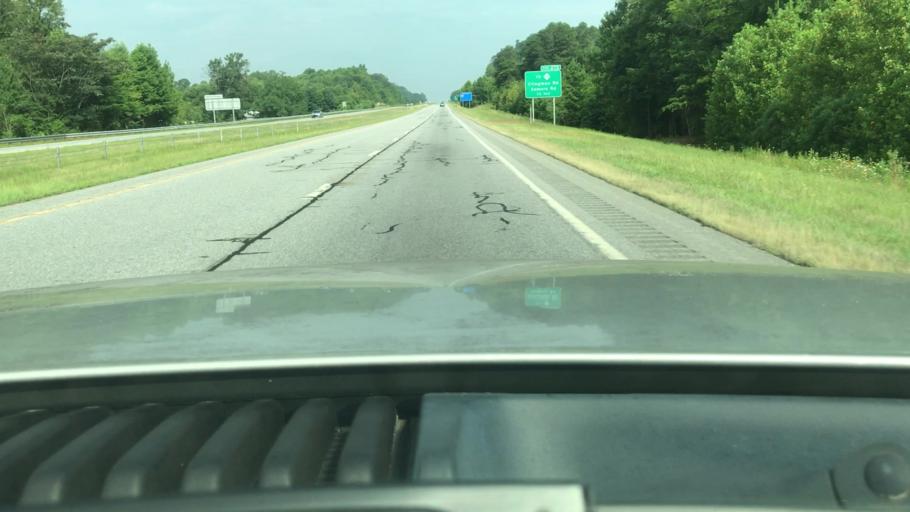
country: US
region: North Carolina
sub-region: Yadkin County
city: Jonesville
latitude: 36.1482
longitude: -80.9175
